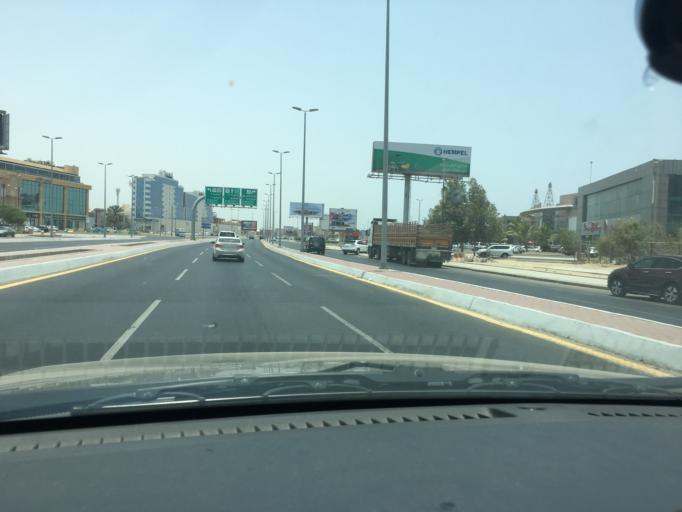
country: SA
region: Makkah
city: Jeddah
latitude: 21.6007
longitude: 39.1435
